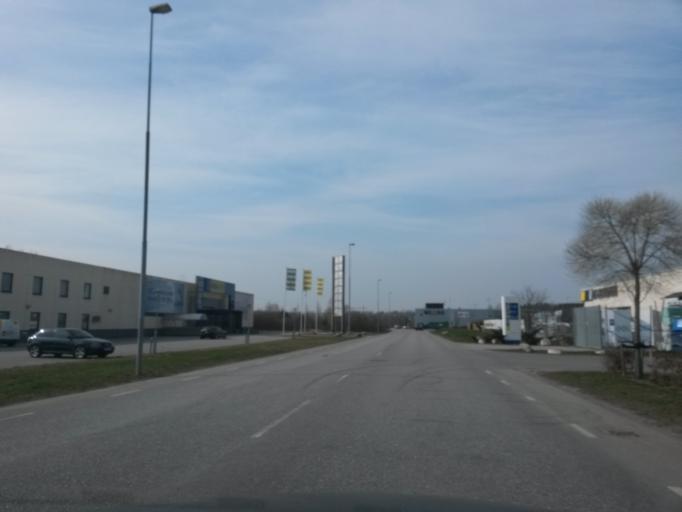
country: SE
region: OErebro
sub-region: Kumla Kommun
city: Kumla
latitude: 59.2091
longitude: 15.1393
